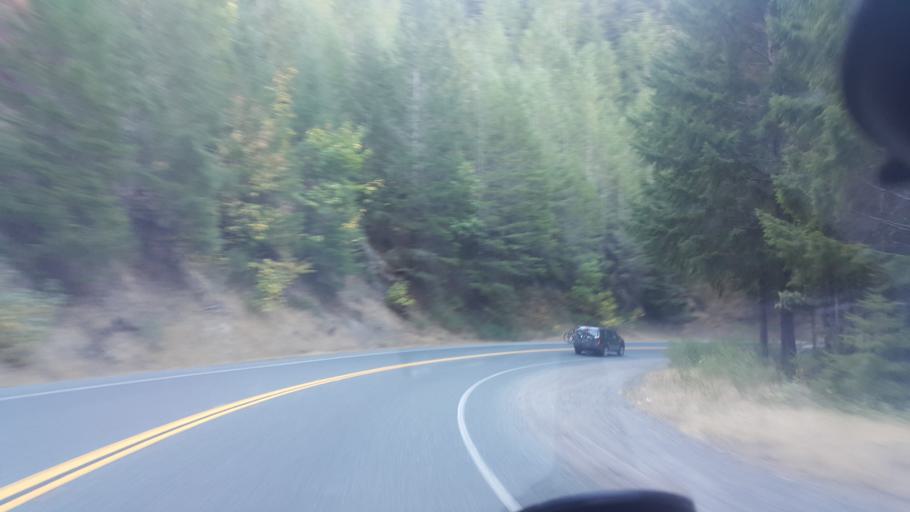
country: US
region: California
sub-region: Mendocino County
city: Brooktrails
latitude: 39.3533
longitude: -123.5093
